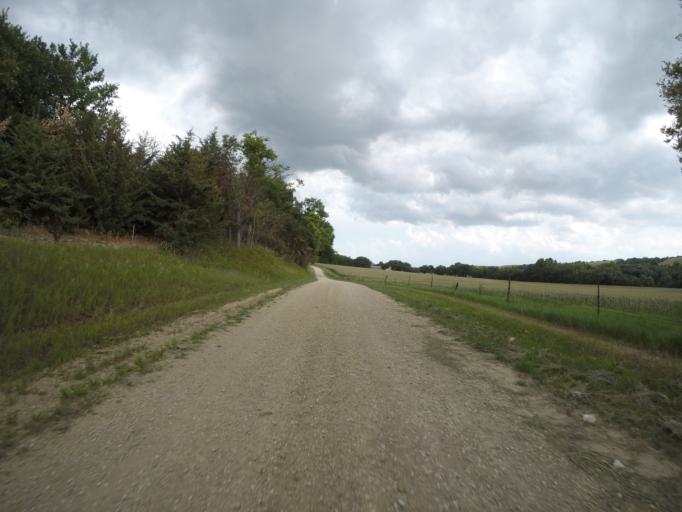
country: US
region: Kansas
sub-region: Marshall County
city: Blue Rapids
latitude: 39.4991
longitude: -96.8326
